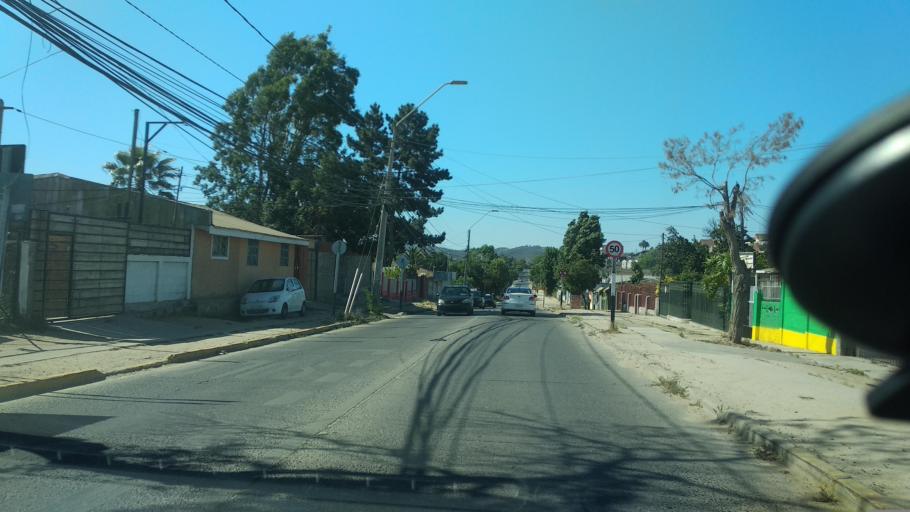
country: CL
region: Valparaiso
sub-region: Provincia de Marga Marga
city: Villa Alemana
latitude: -33.0561
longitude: -71.3735
